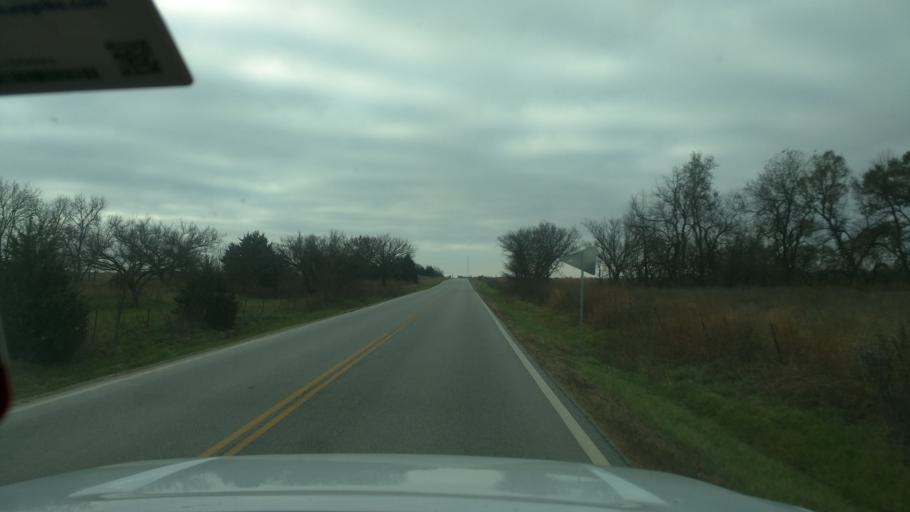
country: US
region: Kansas
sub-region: Greenwood County
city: Eureka
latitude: 37.6577
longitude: -96.2346
